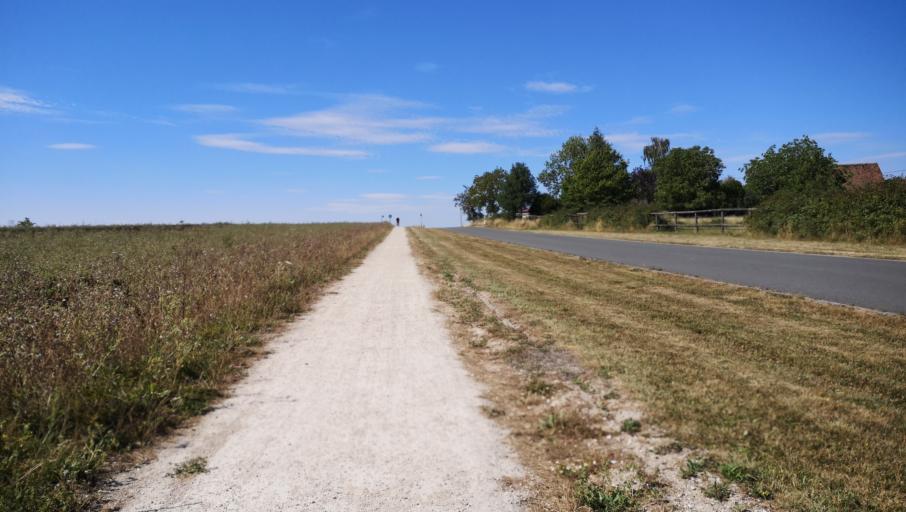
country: FR
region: Centre
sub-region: Departement du Loiret
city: Marigny-les-Usages
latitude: 47.9524
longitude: 2.0076
